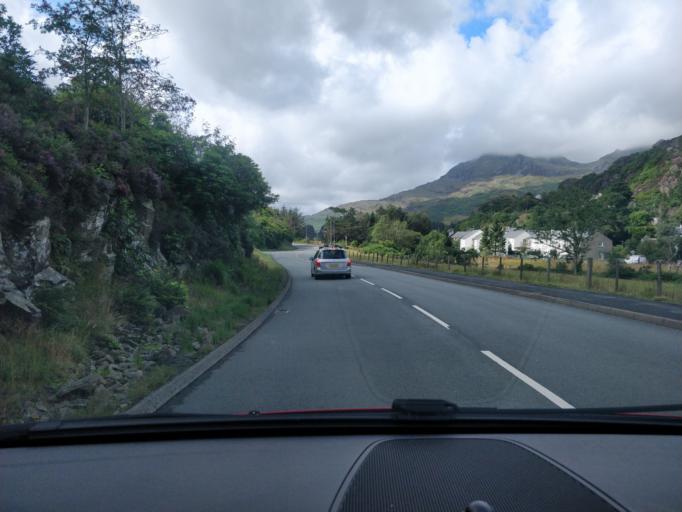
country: GB
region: Wales
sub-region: Gwynedd
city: Blaenau-Ffestiniog
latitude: 52.9895
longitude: -3.9515
